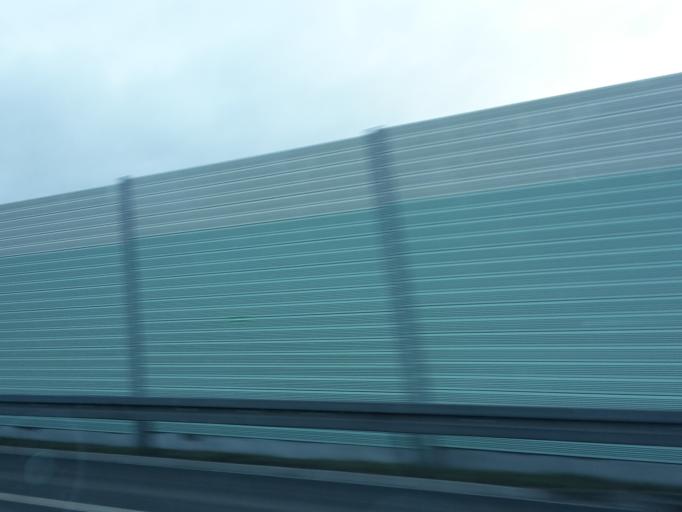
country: PL
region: Warmian-Masurian Voivodeship
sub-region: Powiat ostrodzki
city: Maldyty
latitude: 53.9807
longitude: 19.6966
